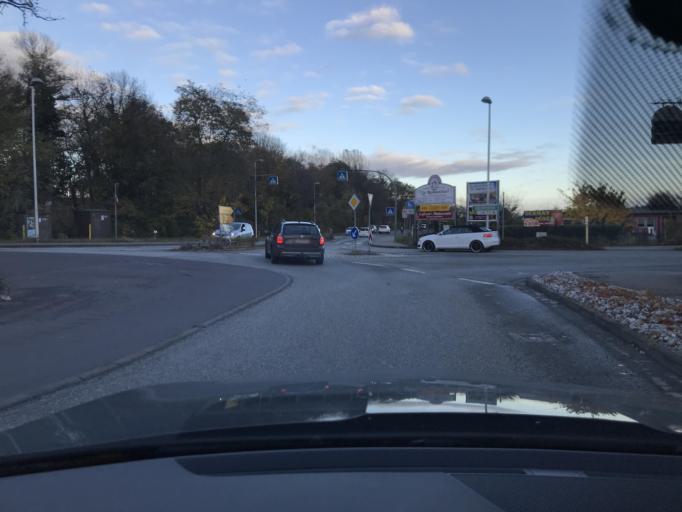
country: DE
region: Saxony-Anhalt
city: Thale
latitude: 51.7538
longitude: 11.0458
